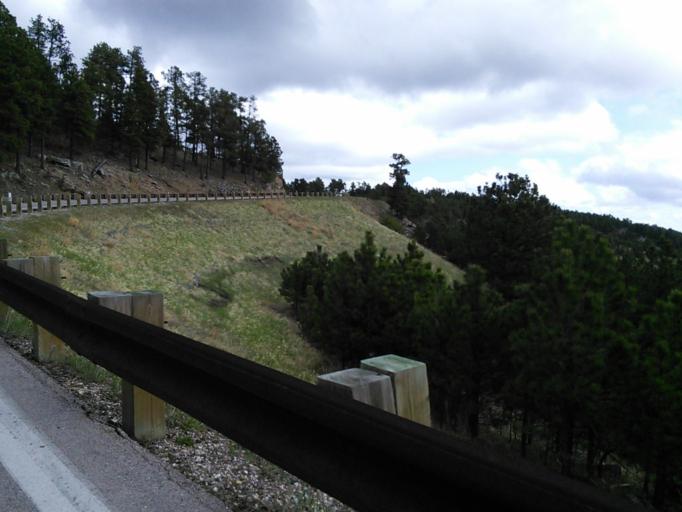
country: US
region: South Dakota
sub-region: Custer County
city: Custer
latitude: 43.7446
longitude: -103.4761
